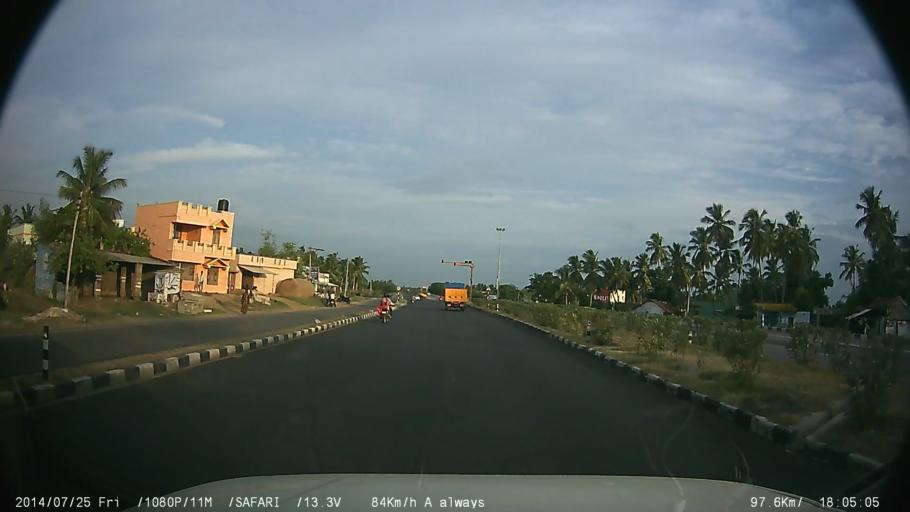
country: IN
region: Tamil Nadu
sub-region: Krishnagiri
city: Kaverippattanam
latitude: 12.4428
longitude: 78.2186
